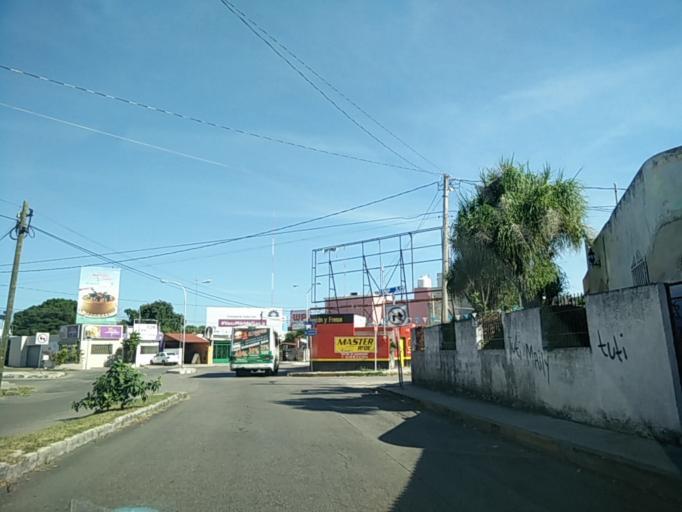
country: MX
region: Yucatan
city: Merida
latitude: 20.9969
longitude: -89.6030
